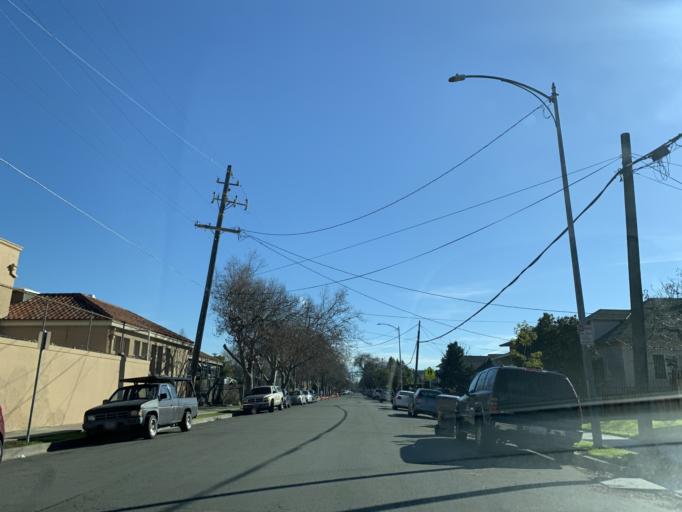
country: US
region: California
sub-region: Santa Clara County
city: San Jose
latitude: 37.3225
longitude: -121.8877
